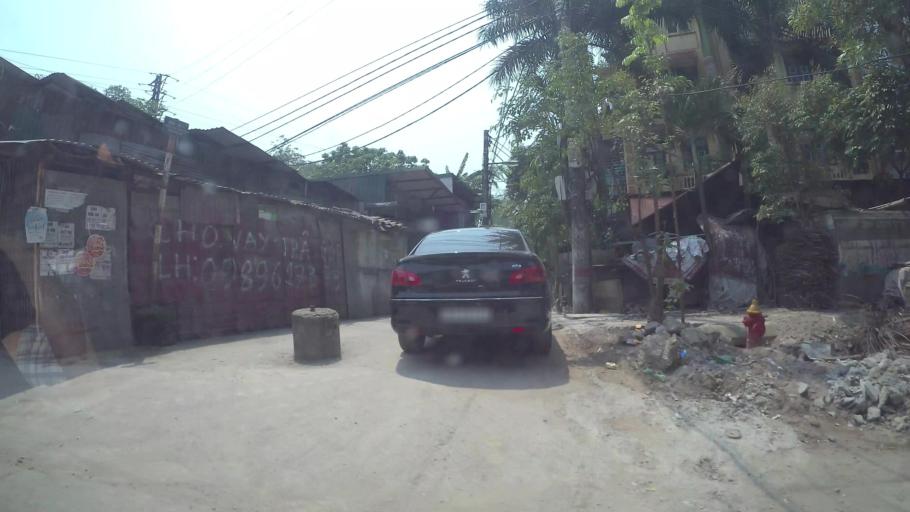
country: VN
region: Ha Noi
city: Van Dien
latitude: 20.9487
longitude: 105.8249
